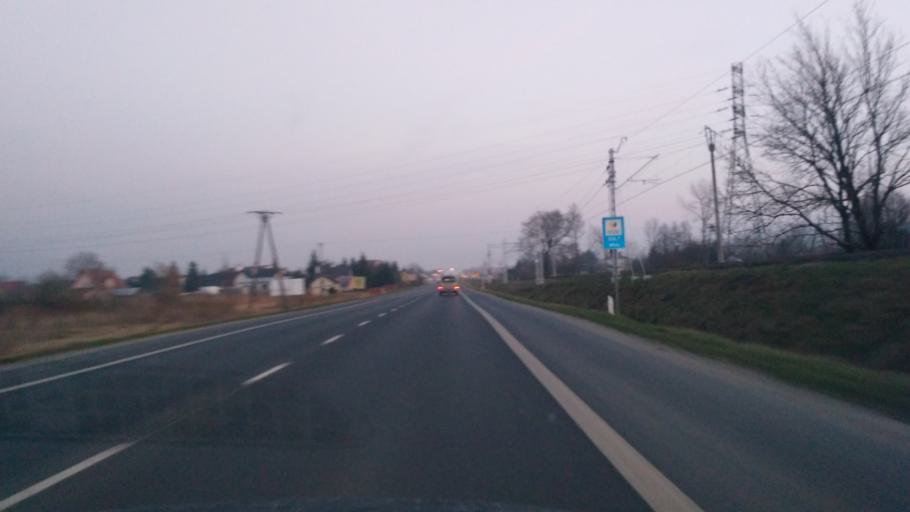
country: PL
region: Subcarpathian Voivodeship
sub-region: Powiat rzeszowski
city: Rudna Mala
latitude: 50.0918
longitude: 21.9815
